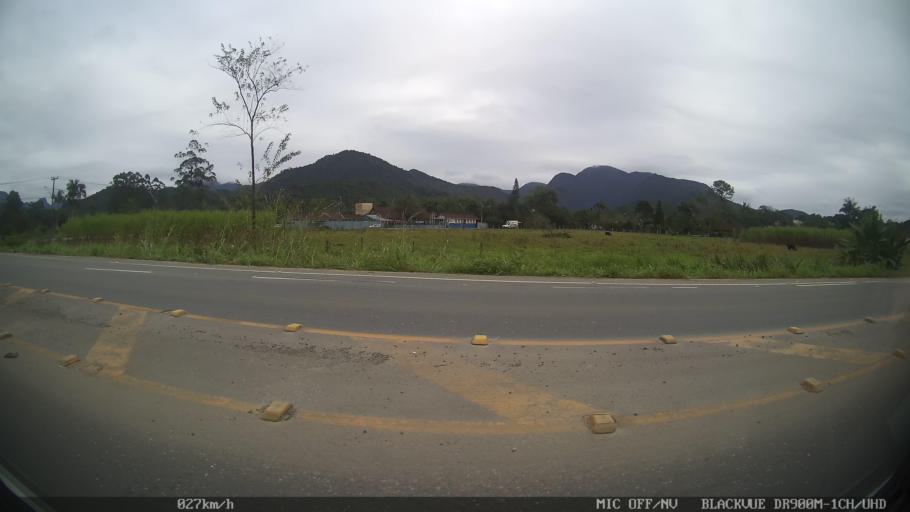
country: BR
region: Santa Catarina
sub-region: Joinville
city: Joinville
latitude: -26.2683
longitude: -48.9229
